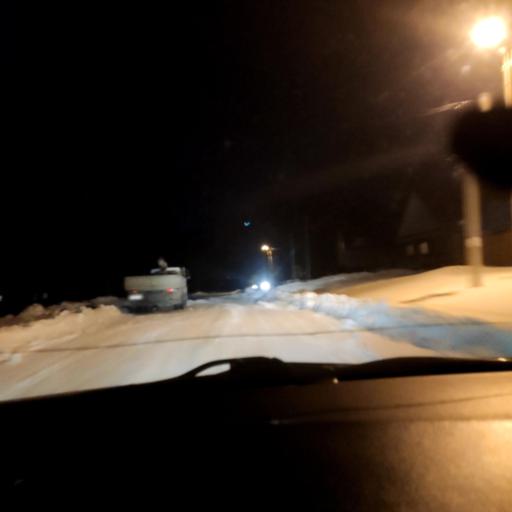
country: RU
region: Bashkortostan
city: Kabakovo
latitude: 54.6719
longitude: 56.2151
